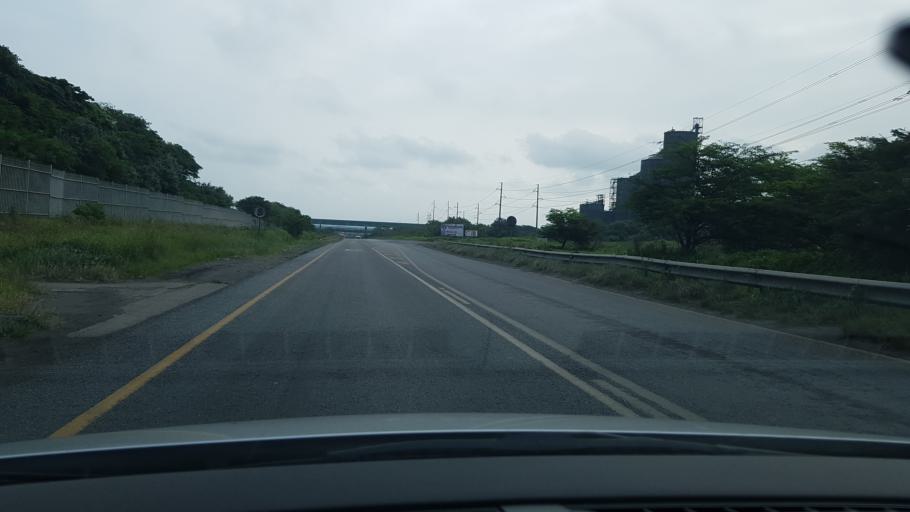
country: ZA
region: KwaZulu-Natal
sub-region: uThungulu District Municipality
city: Richards Bay
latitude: -28.7738
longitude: 32.0325
